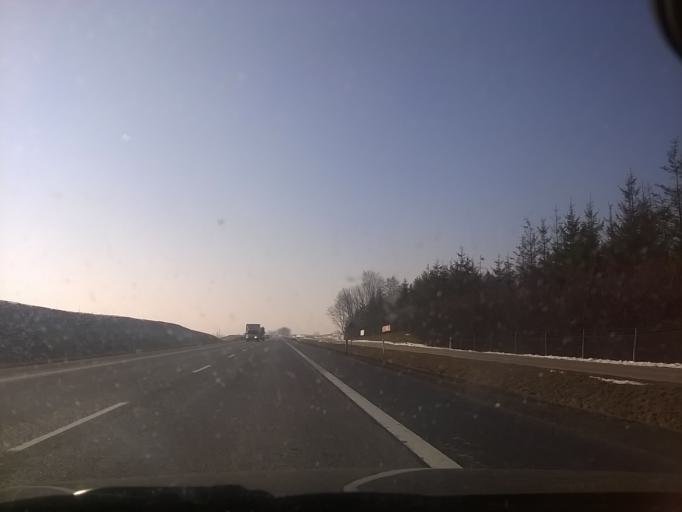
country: PL
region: Warmian-Masurian Voivodeship
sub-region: Powiat olsztynski
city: Biskupiec
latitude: 53.8429
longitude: 20.9399
